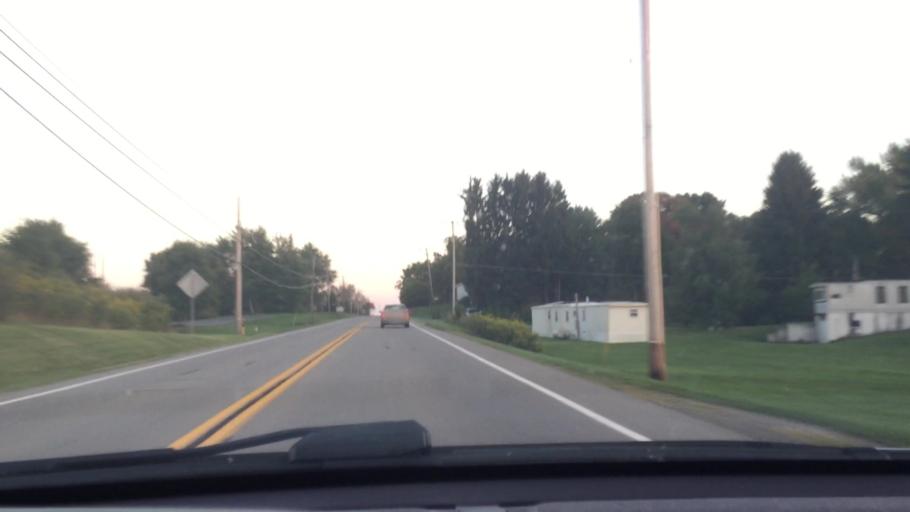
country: US
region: Pennsylvania
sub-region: Mercer County
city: Grove City
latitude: 41.1418
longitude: -80.0800
